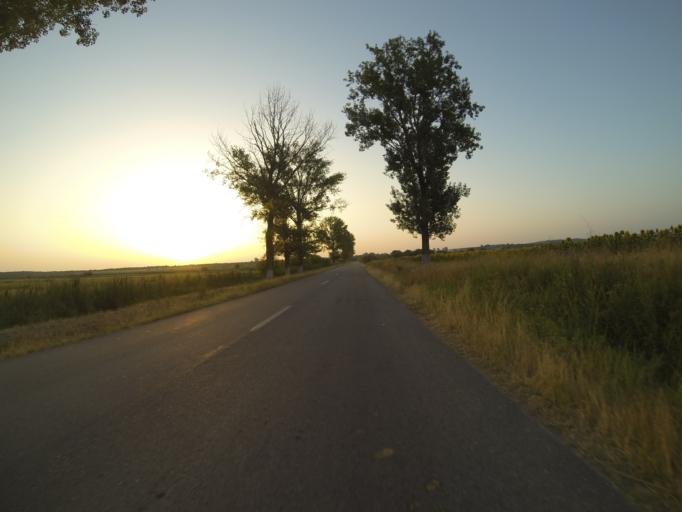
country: RO
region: Dolj
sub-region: Comuna Dobresti
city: Dobresti
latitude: 43.9828
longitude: 23.9265
